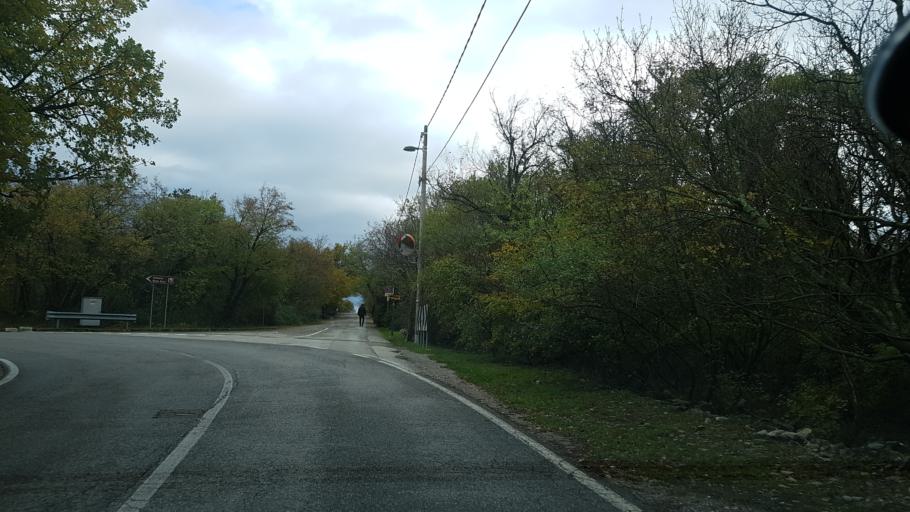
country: IT
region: Friuli Venezia Giulia
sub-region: Provincia di Trieste
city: Prosecco-Contovello
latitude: 45.6997
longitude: 13.7402
